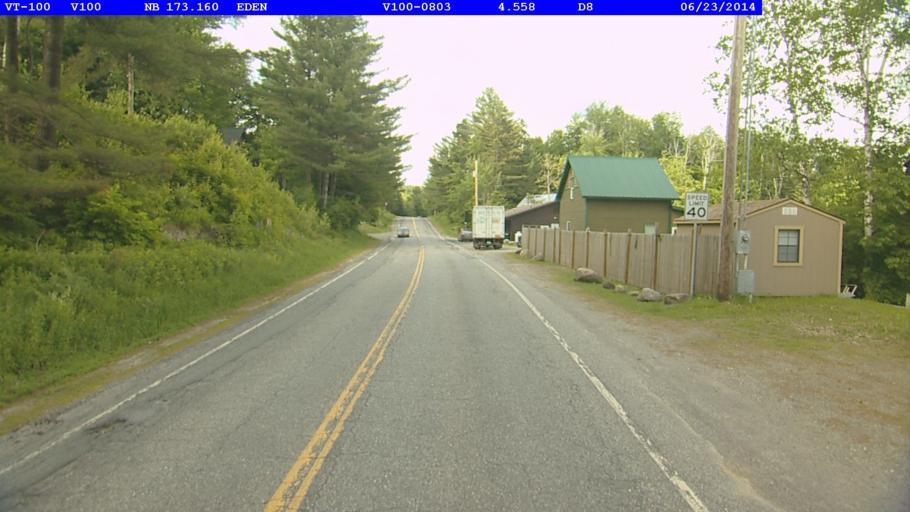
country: US
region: Vermont
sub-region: Lamoille County
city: Hyde Park
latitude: 44.7159
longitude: -72.5153
